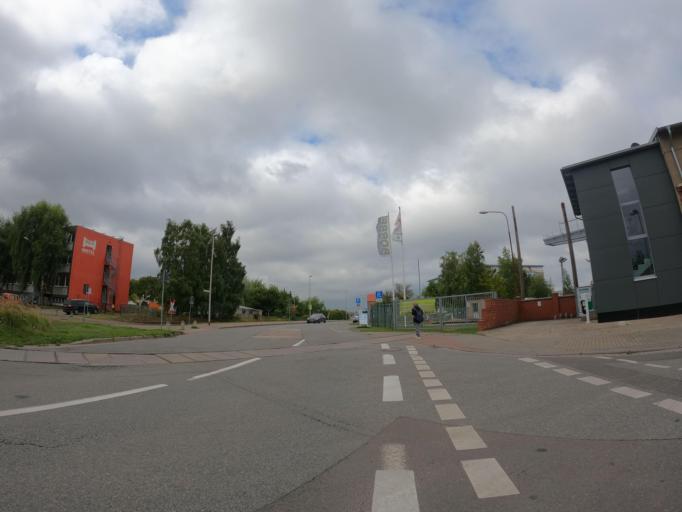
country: DE
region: Mecklenburg-Vorpommern
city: Stralsund
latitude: 54.3087
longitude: 13.1035
